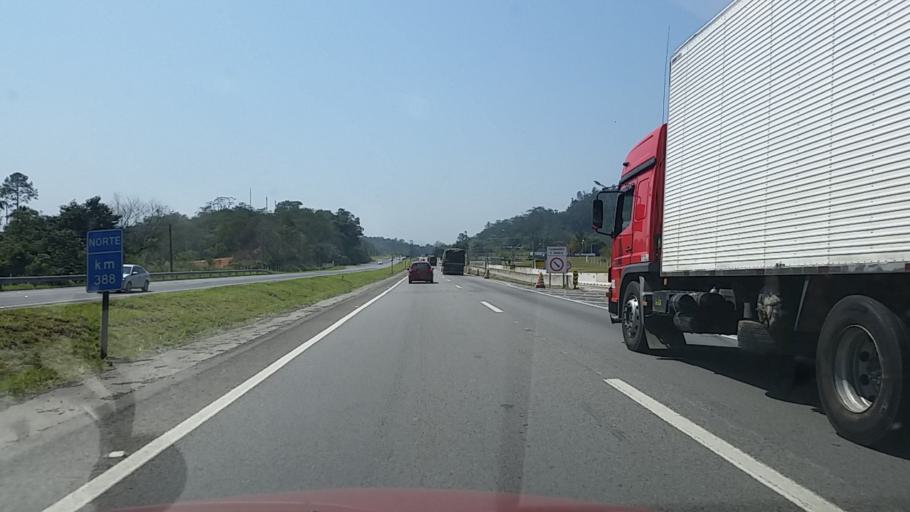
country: BR
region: Sao Paulo
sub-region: Miracatu
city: Miracatu
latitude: -24.2695
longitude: -47.3982
